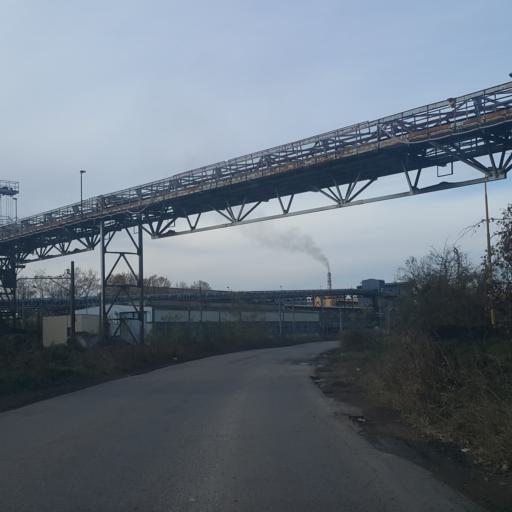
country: RS
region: Central Serbia
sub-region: Belgrade
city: Lazarevac
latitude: 44.4243
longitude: 20.2874
